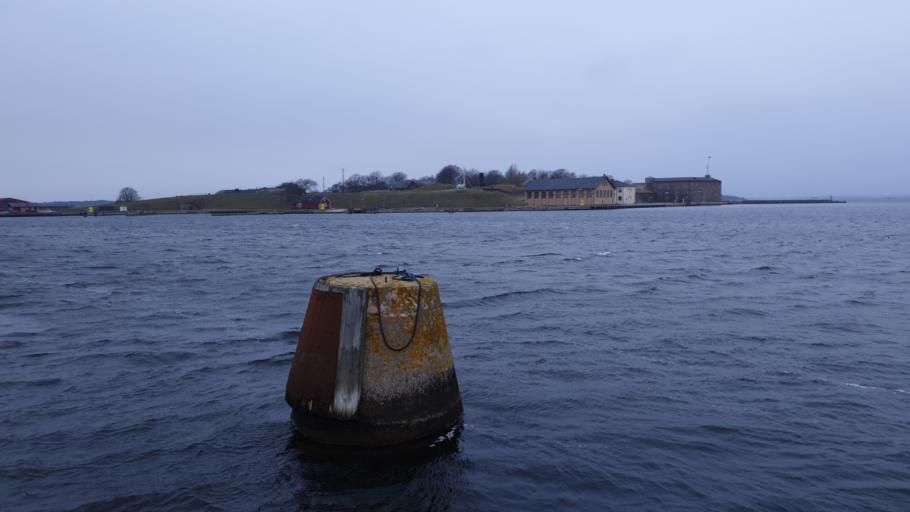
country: SE
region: Blekinge
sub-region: Karlskrona Kommun
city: Karlskrona
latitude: 56.1059
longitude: 15.5949
